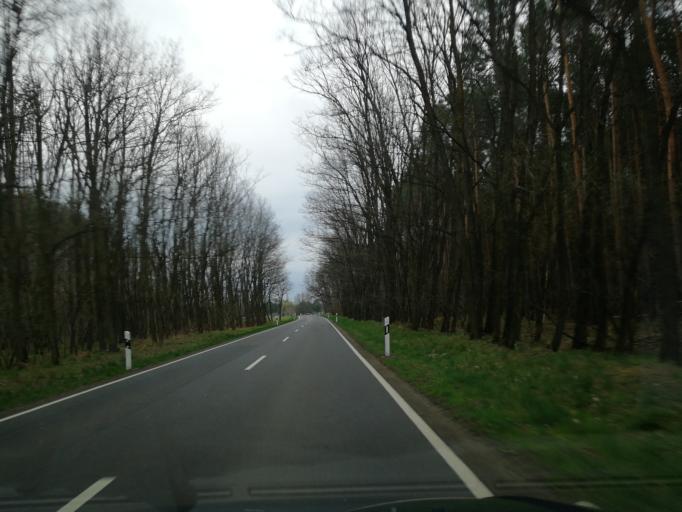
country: DE
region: Brandenburg
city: Vetschau
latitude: 51.7698
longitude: 14.0665
